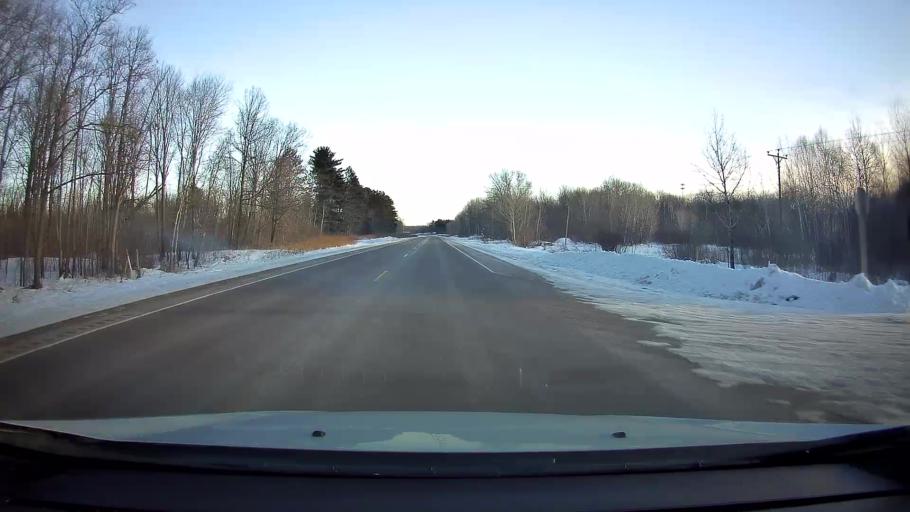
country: US
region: Wisconsin
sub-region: Washburn County
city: Shell Lake
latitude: 45.7033
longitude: -91.9528
